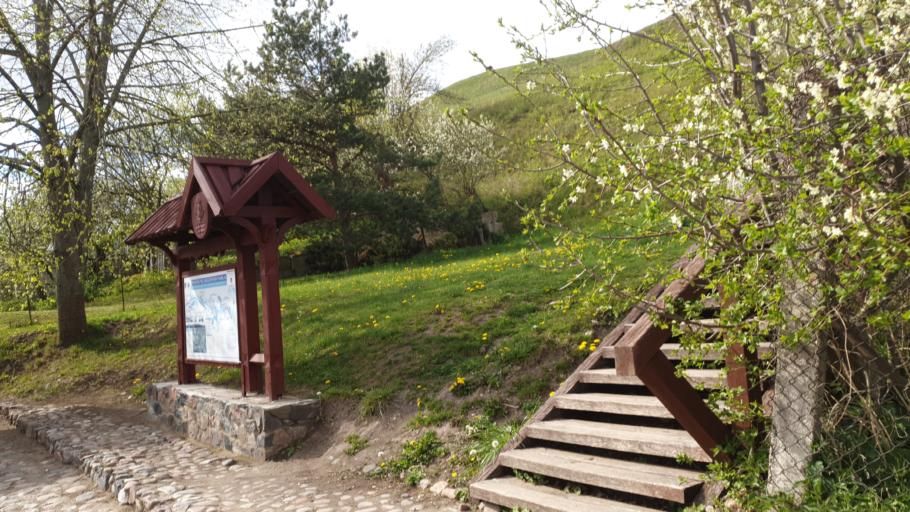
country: LT
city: Vilkija
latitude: 55.0794
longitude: 23.4075
